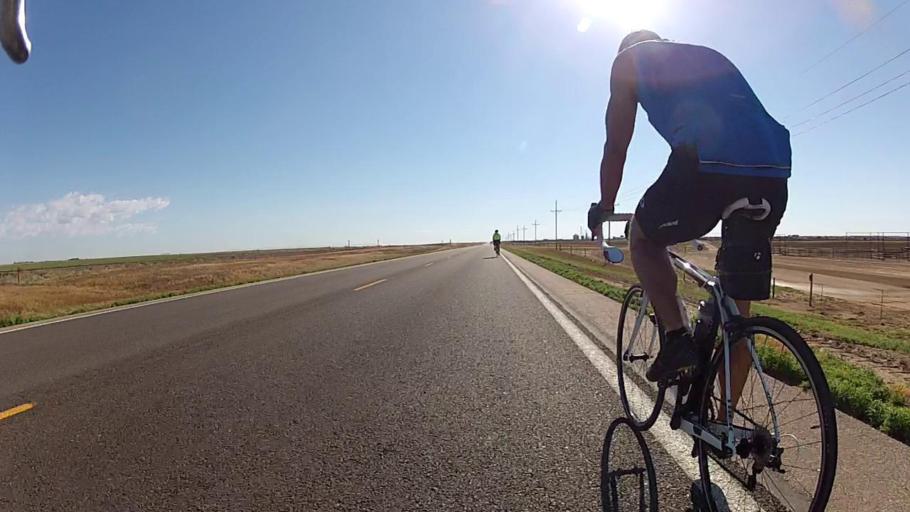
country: US
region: Kansas
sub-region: Gray County
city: Cimarron
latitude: 37.5688
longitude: -100.5450
